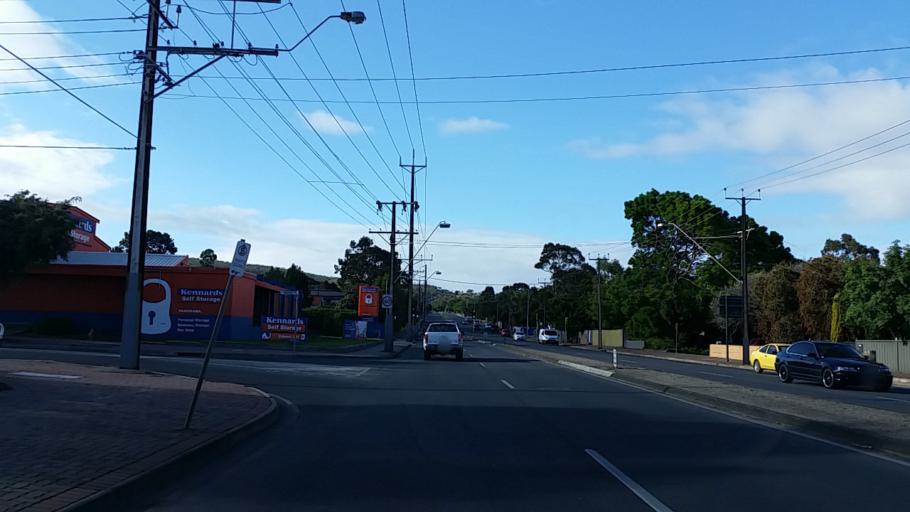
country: AU
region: South Australia
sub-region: Mitcham
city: Clapham
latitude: -34.9924
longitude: 138.5928
